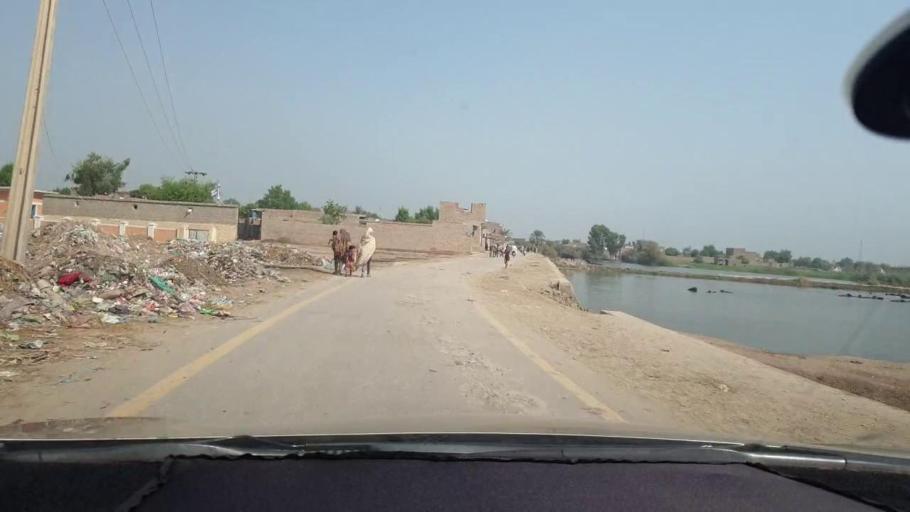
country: PK
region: Sindh
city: Kambar
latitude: 27.5777
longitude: 68.0068
